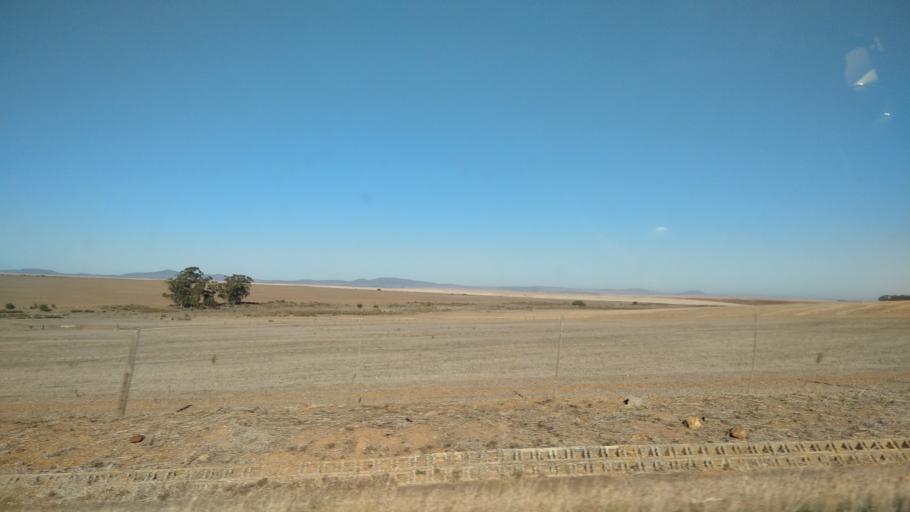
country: ZA
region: Western Cape
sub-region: West Coast District Municipality
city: Malmesbury
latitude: -33.3383
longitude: 18.6349
